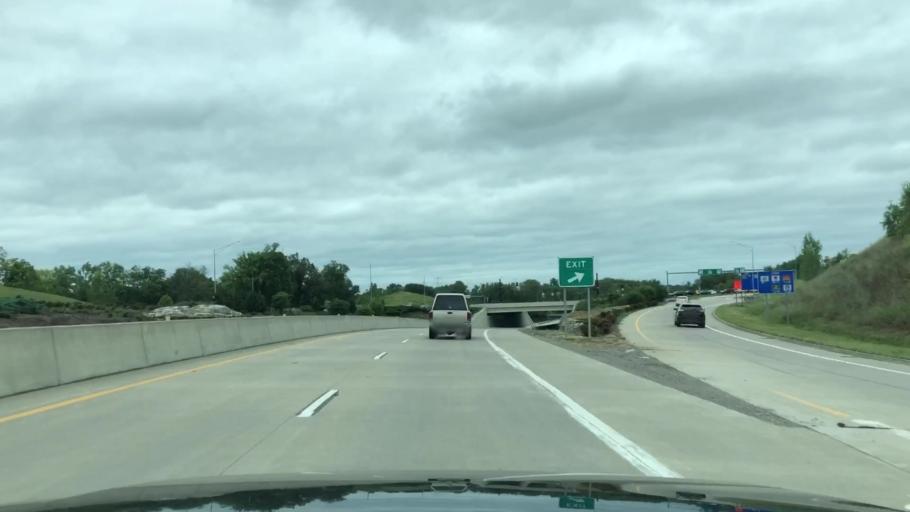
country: US
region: Missouri
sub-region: Saint Louis County
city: Maryland Heights
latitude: 38.6836
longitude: -90.4937
